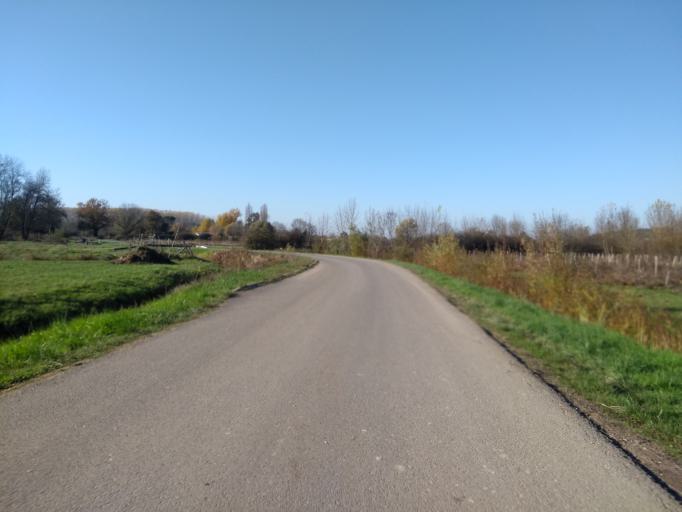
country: FR
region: Aquitaine
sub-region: Departement de la Gironde
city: Cambes
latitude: 44.7194
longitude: -0.4637
